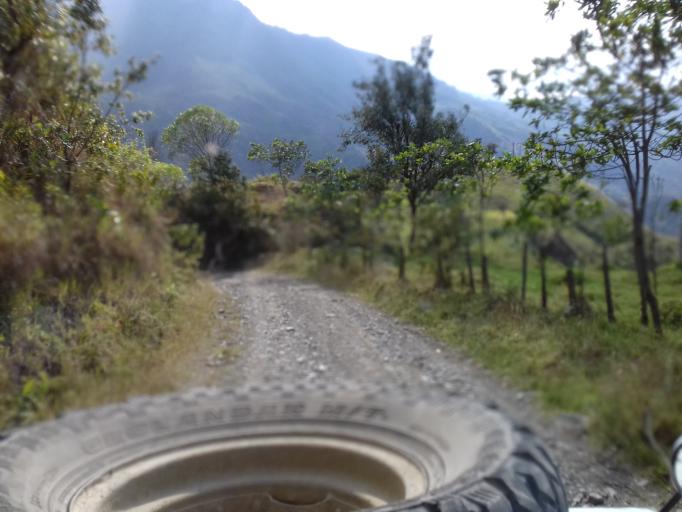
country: CO
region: Tolima
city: Cajamarca
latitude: 4.5309
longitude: -75.4160
